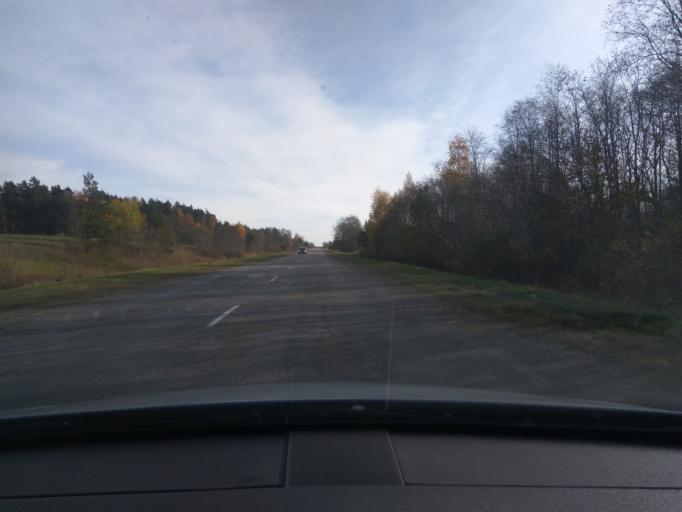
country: LV
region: Alsunga
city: Alsunga
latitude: 57.0035
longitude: 21.7417
